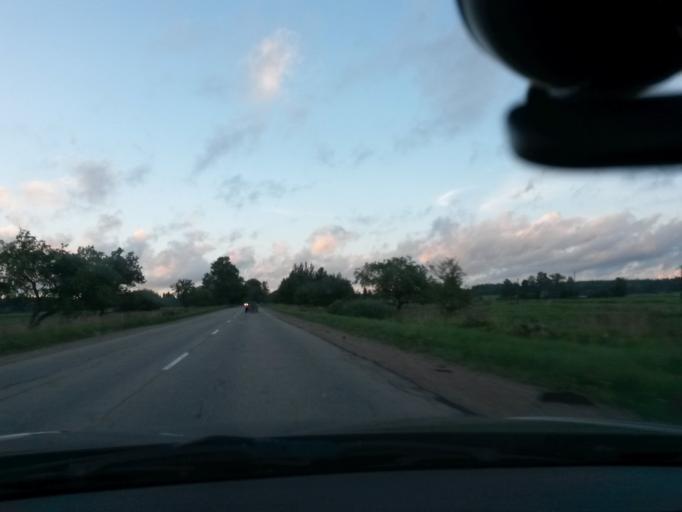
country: LV
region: Jekabpils Rajons
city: Jekabpils
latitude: 56.7175
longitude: 25.9891
